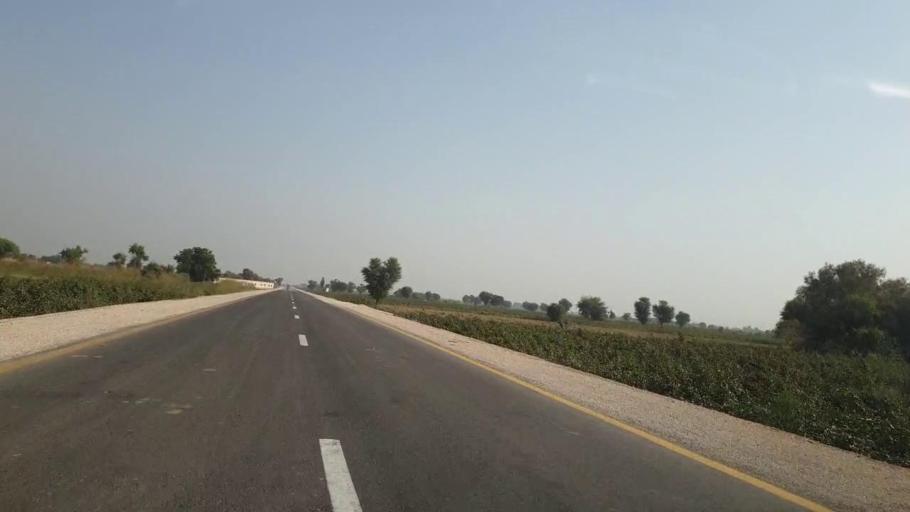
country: PK
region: Sindh
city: Sehwan
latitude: 26.4718
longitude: 67.7911
